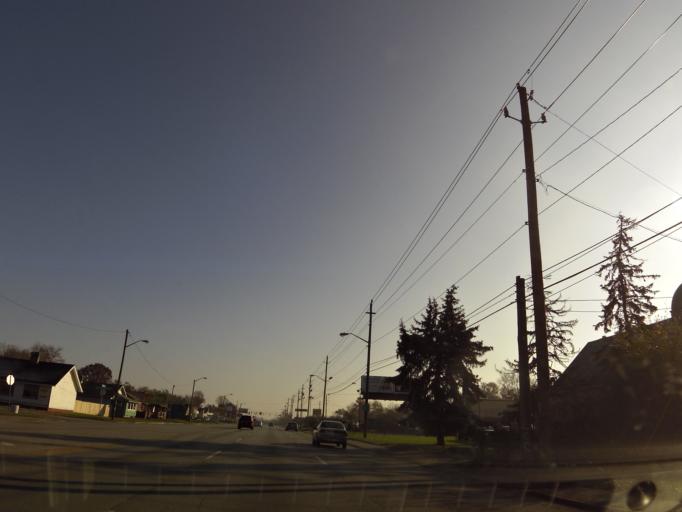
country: US
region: Indiana
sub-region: Marion County
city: Speedway
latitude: 39.7878
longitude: -86.2143
